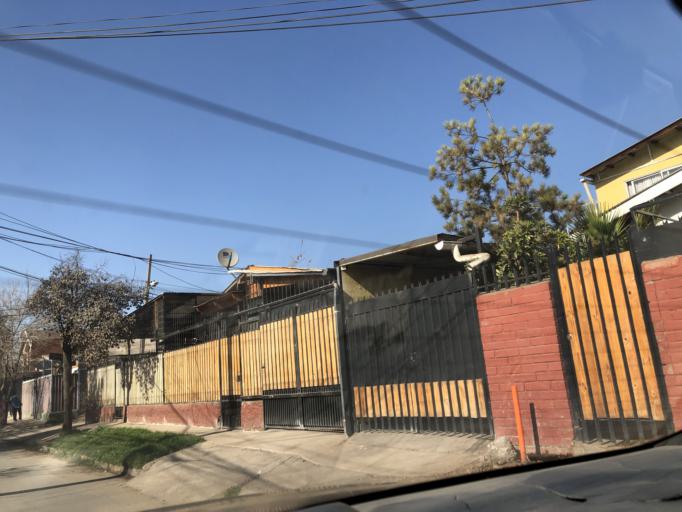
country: CL
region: Santiago Metropolitan
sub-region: Provincia de Cordillera
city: Puente Alto
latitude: -33.5782
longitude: -70.5896
